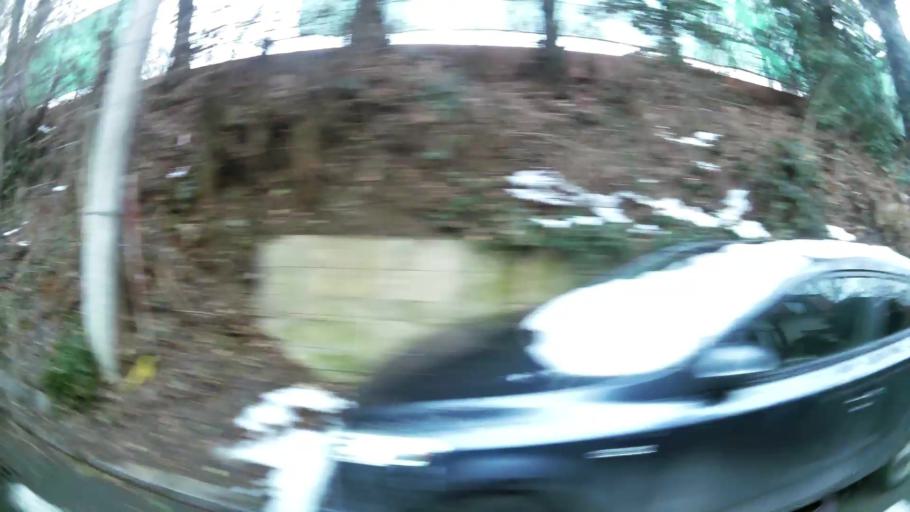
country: RS
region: Central Serbia
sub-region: Belgrade
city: Novi Beograd
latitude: 44.7930
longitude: 20.4317
